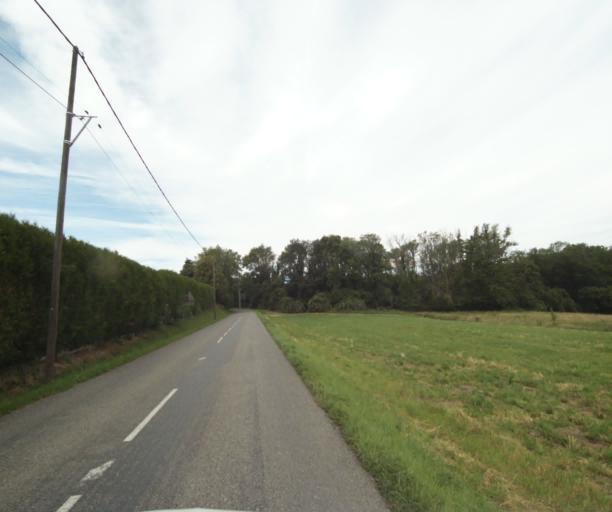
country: FR
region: Rhone-Alpes
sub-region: Departement de la Haute-Savoie
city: Allinges
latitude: 46.3502
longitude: 6.4506
